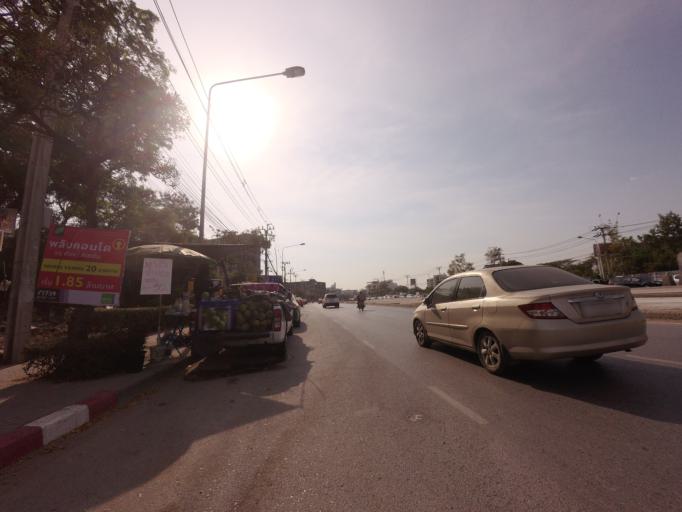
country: TH
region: Bangkok
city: Bang Kapi
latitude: 13.7520
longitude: 100.6397
